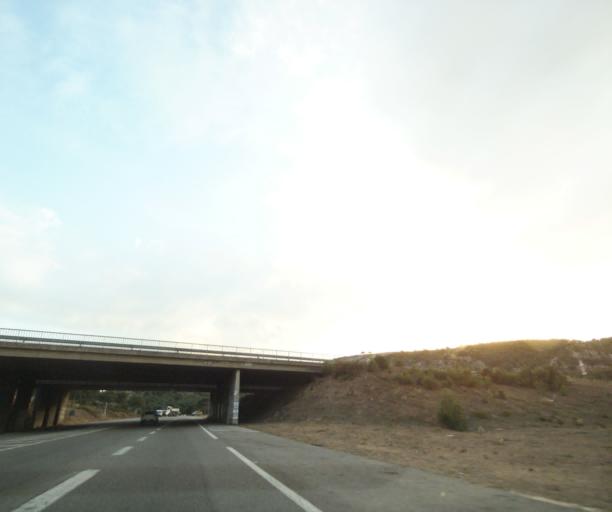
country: FR
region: Provence-Alpes-Cote d'Azur
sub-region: Departement des Bouches-du-Rhone
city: Chateauneuf-les-Martigues
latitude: 43.3737
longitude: 5.1856
